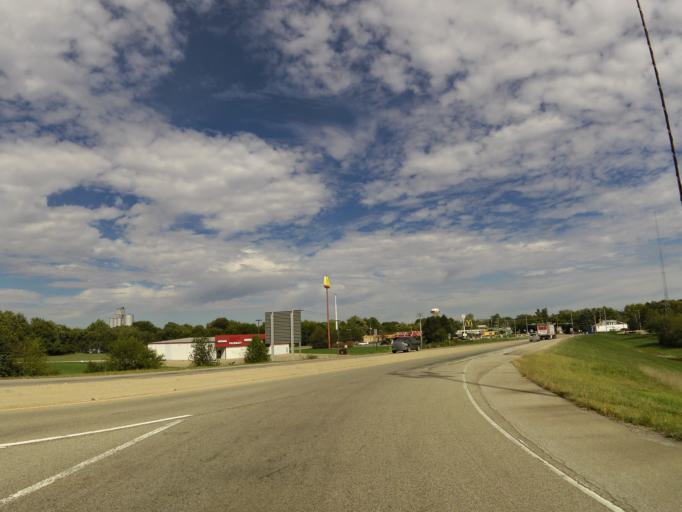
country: US
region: Illinois
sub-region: McLean County
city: Le Roy
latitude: 40.3401
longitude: -88.7633
